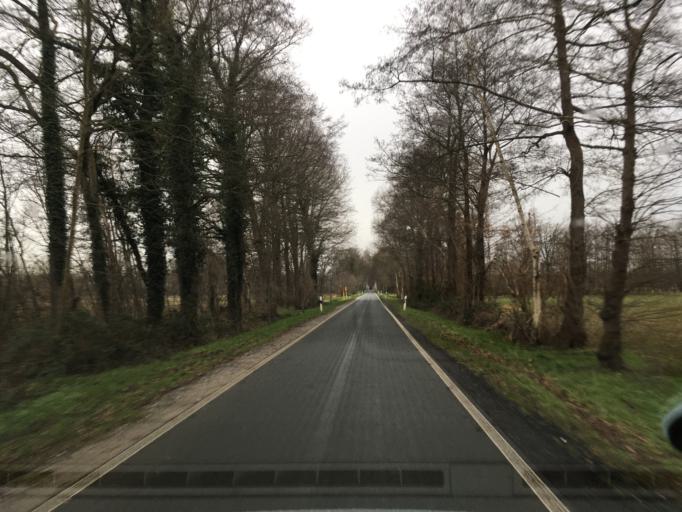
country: DE
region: North Rhine-Westphalia
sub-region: Regierungsbezirk Munster
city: Heek
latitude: 52.1375
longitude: 7.1360
